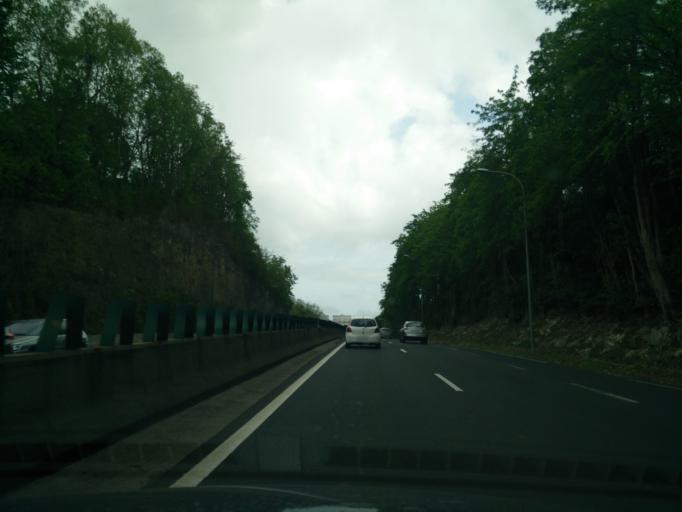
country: GP
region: Guadeloupe
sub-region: Guadeloupe
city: Pointe-a-Pitre
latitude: 16.2379
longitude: -61.5230
